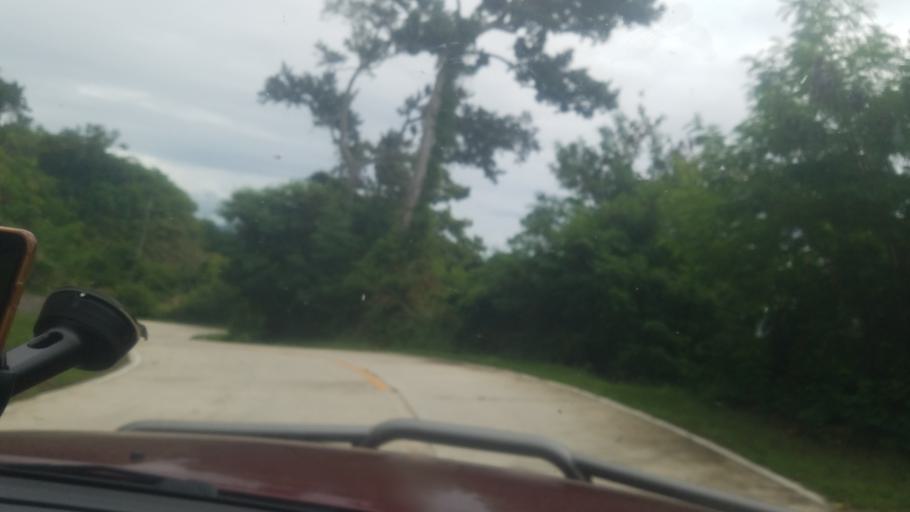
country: PH
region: Cagayan Valley
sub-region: Province of Quirino
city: Nagtipunan
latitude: 16.0441
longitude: 121.7161
